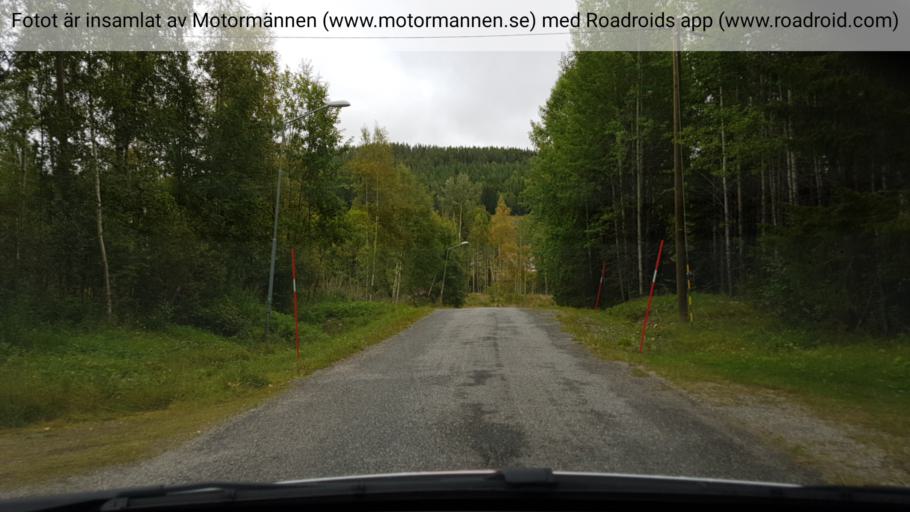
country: SE
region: Vaesterbotten
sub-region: Dorotea Kommun
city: Dorotea
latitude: 63.8582
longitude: 16.3570
